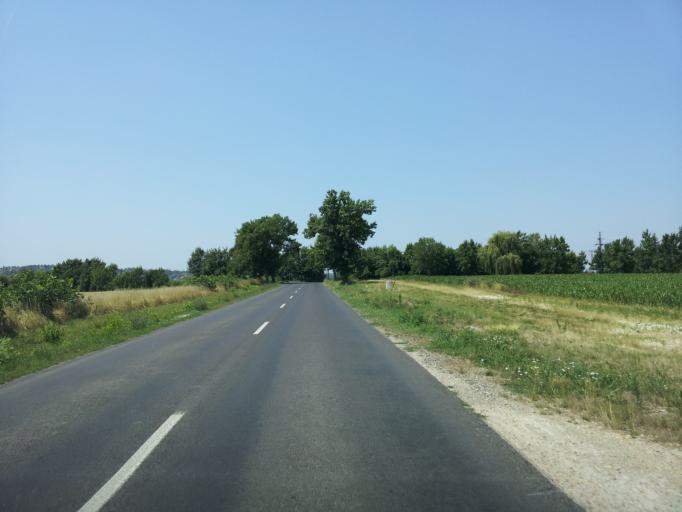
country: HU
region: Zala
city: Zalaegerszeg
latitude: 46.8576
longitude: 16.8377
